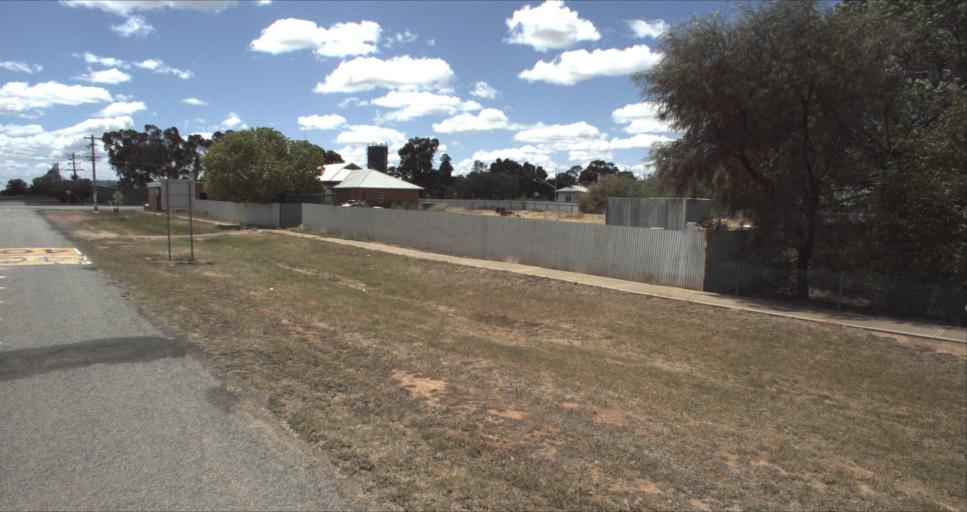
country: AU
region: New South Wales
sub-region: Murrumbidgee Shire
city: Darlington Point
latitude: -34.5184
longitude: 146.1804
